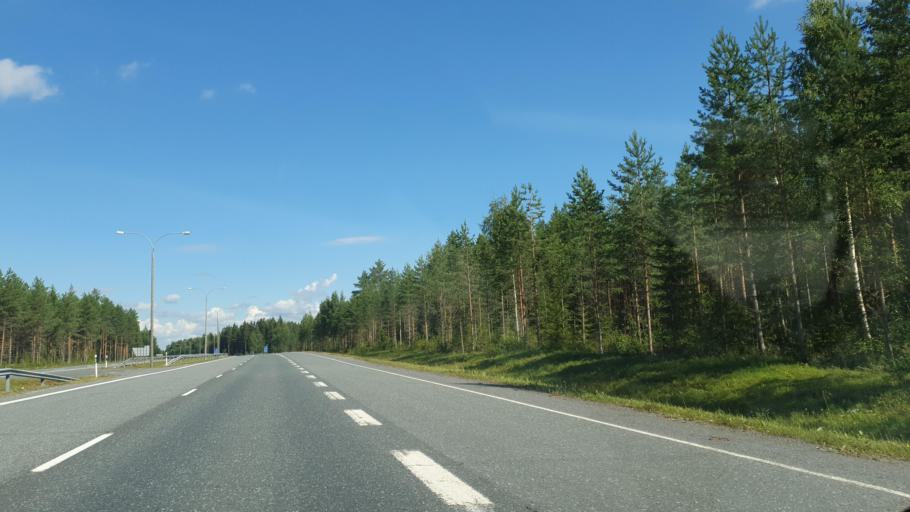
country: FI
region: Northern Savo
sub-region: Ylae-Savo
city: Iisalmi
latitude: 63.5507
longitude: 27.2541
